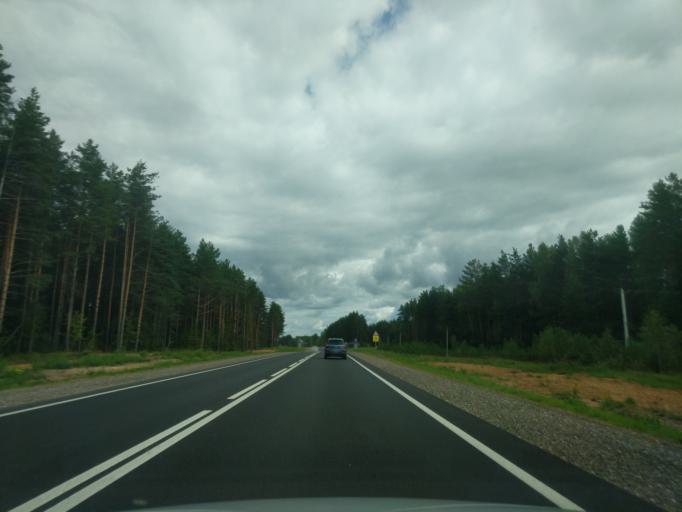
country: RU
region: Jaroslavl
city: Tunoshna
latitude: 57.5702
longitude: 40.2657
